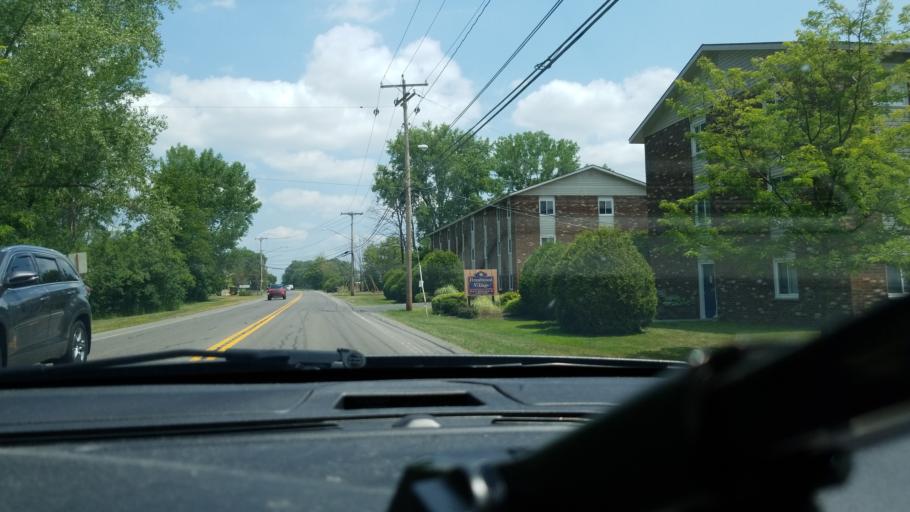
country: US
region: New York
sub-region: Onondaga County
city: Galeville
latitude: 43.1086
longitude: -76.1787
